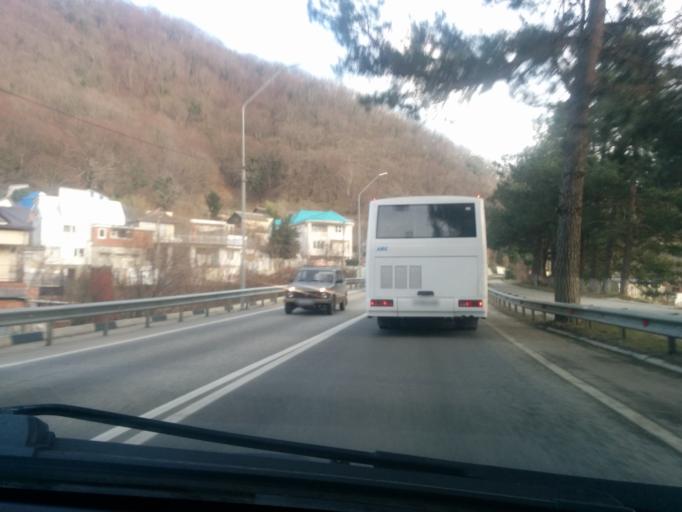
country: RU
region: Krasnodarskiy
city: Ol'ginka
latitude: 44.1976
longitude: 38.8905
